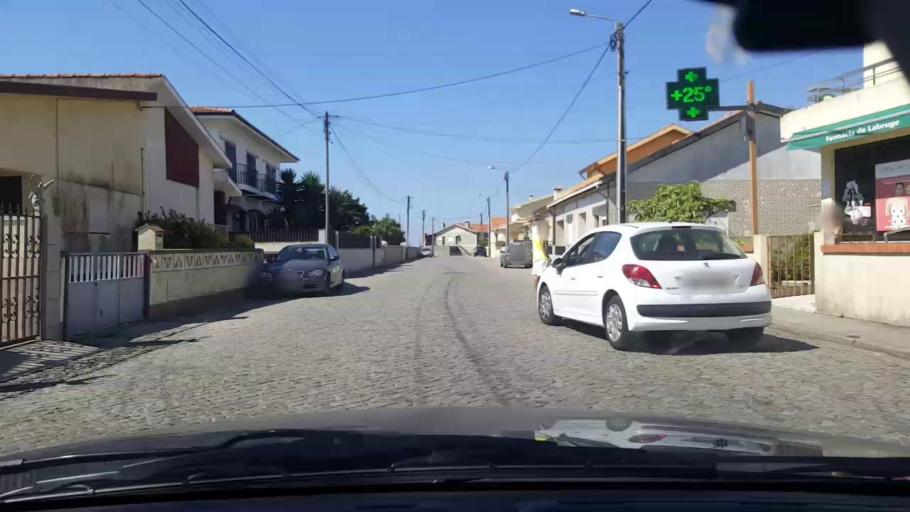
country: PT
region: Porto
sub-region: Matosinhos
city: Lavra
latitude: 41.2794
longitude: -8.7213
